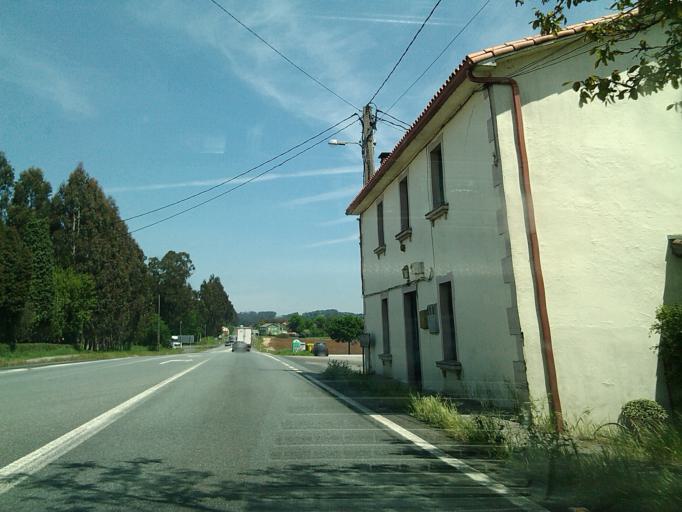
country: ES
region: Galicia
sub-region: Provincia da Coruna
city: Mesia
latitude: 43.0718
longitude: -8.1993
